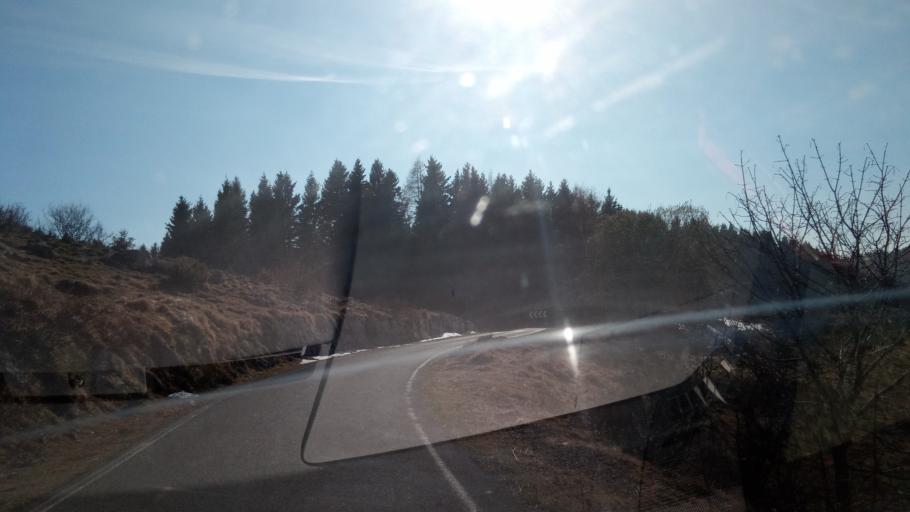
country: IT
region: Veneto
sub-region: Provincia di Treviso
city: Crespano del Grappa
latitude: 45.8527
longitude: 11.7967
